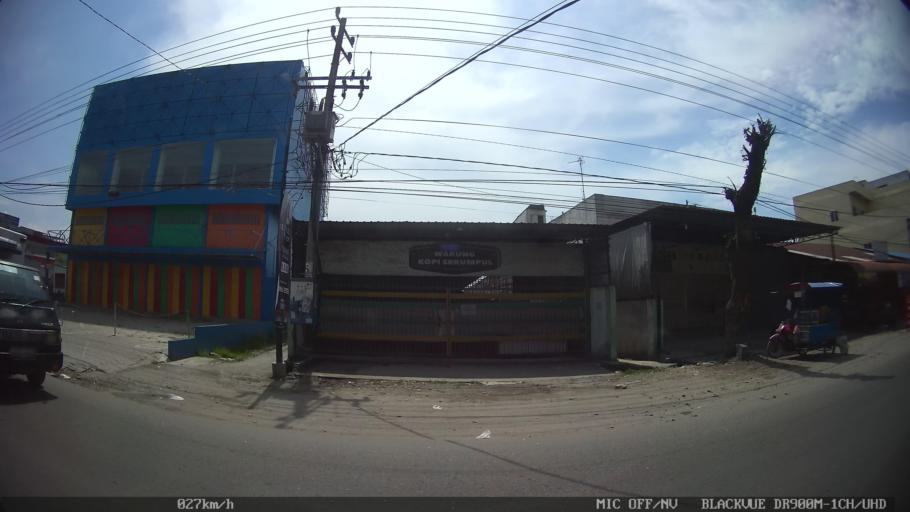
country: ID
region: North Sumatra
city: Labuhan Deli
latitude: 3.6800
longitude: 98.6555
